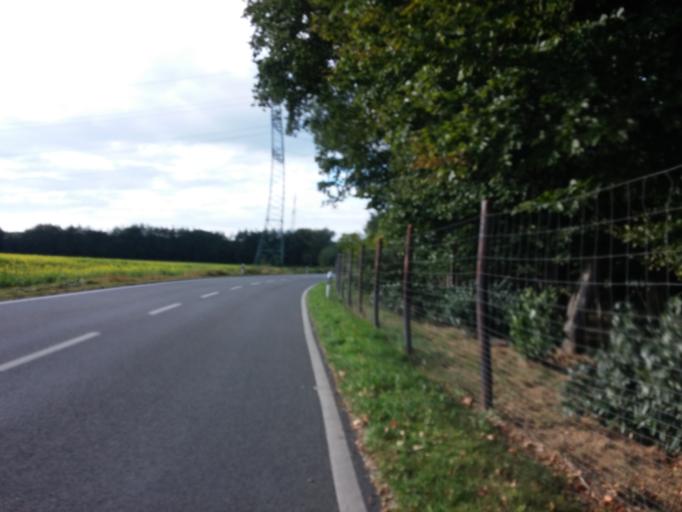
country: DE
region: North Rhine-Westphalia
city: Dorsten
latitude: 51.6210
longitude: 6.9454
